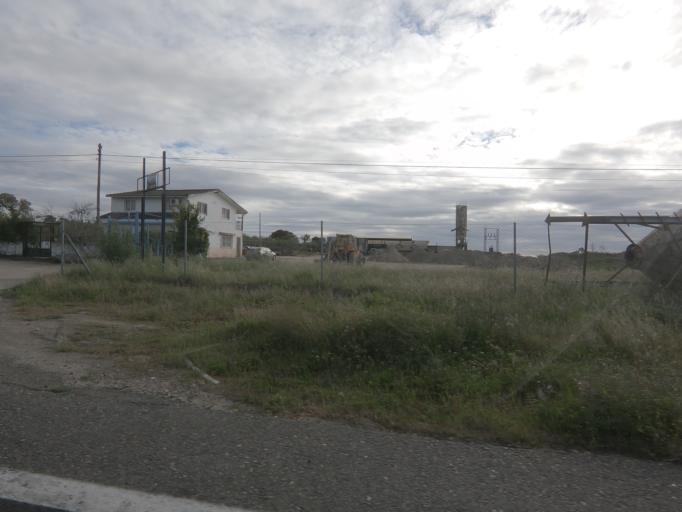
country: ES
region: Extremadura
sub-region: Provincia de Caceres
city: Huelaga
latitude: 40.0389
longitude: -6.6291
